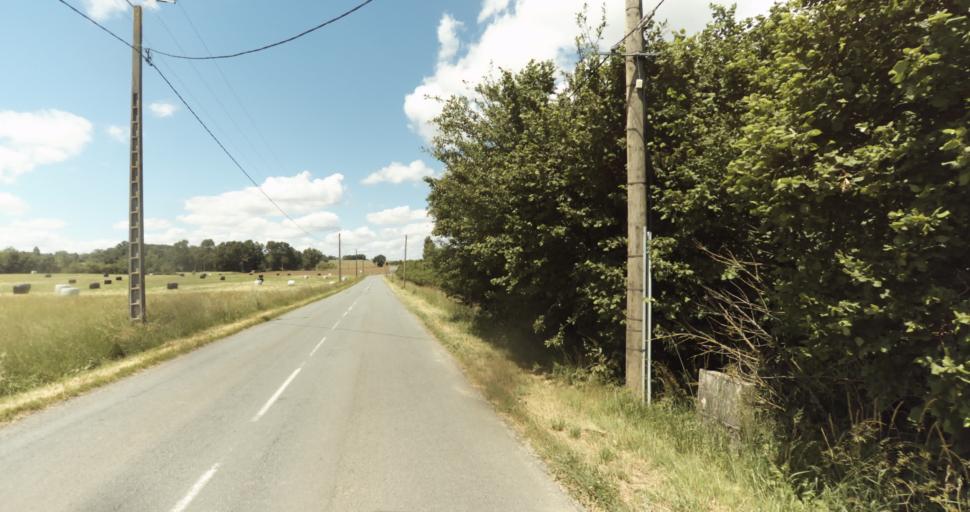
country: FR
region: Aquitaine
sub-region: Departement de la Dordogne
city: Beaumont-du-Perigord
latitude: 44.7179
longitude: 0.7979
